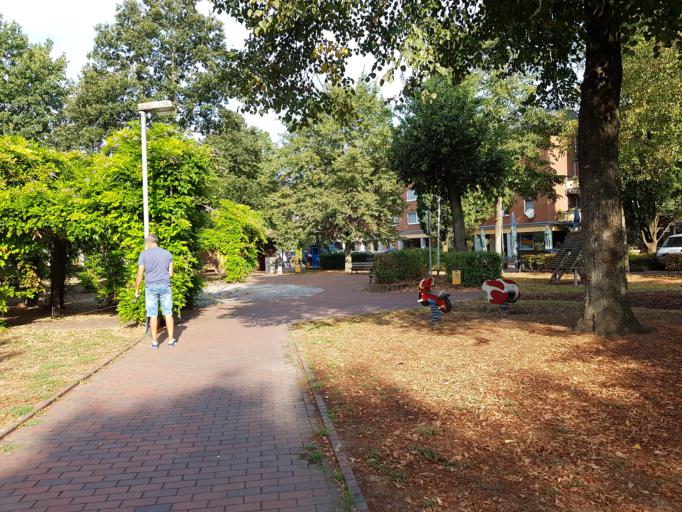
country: DE
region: North Rhine-Westphalia
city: Tonisvorst
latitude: 51.3202
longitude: 6.4985
